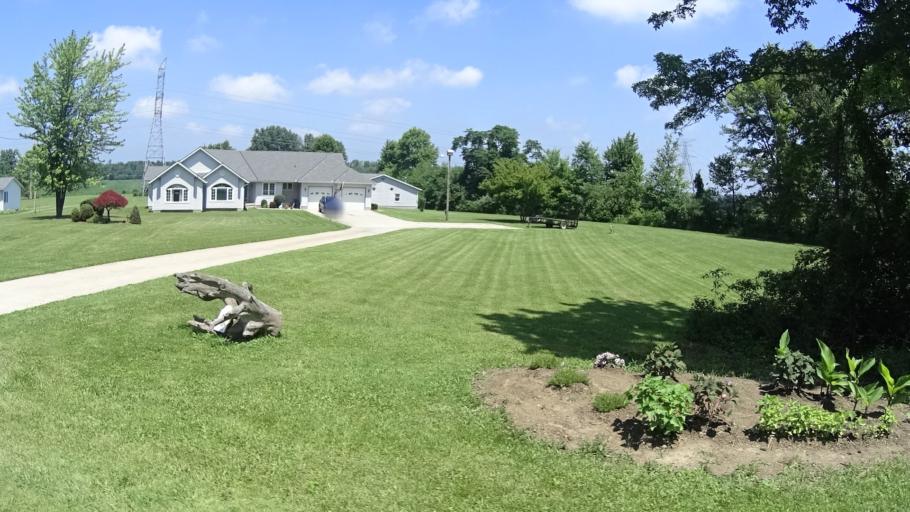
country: US
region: Ohio
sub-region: Lorain County
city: Vermilion
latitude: 41.3403
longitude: -82.3774
